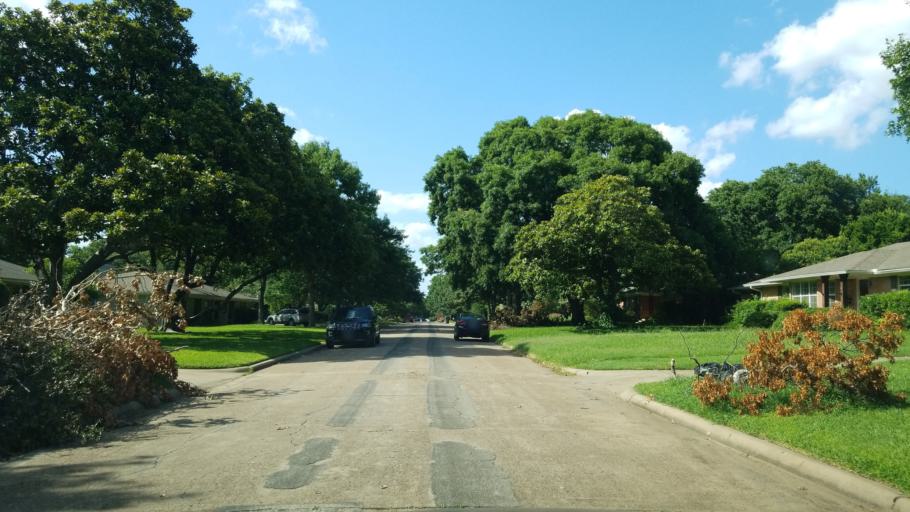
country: US
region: Texas
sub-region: Dallas County
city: University Park
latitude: 32.8847
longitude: -96.8498
